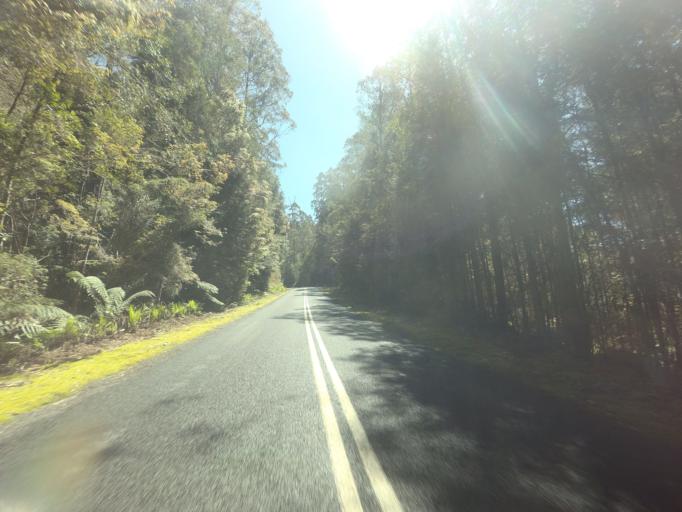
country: AU
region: Tasmania
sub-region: Huon Valley
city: Geeveston
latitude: -42.8202
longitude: 146.3091
